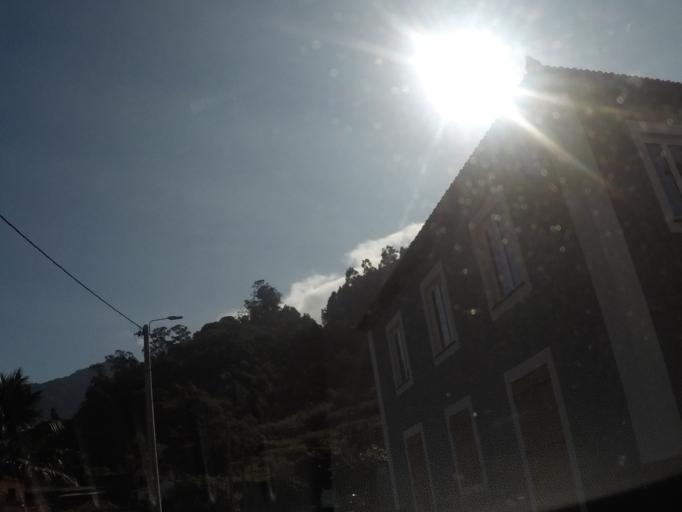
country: PT
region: Madeira
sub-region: Sao Vicente
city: Sao Vicente
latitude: 32.7870
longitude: -17.0360
